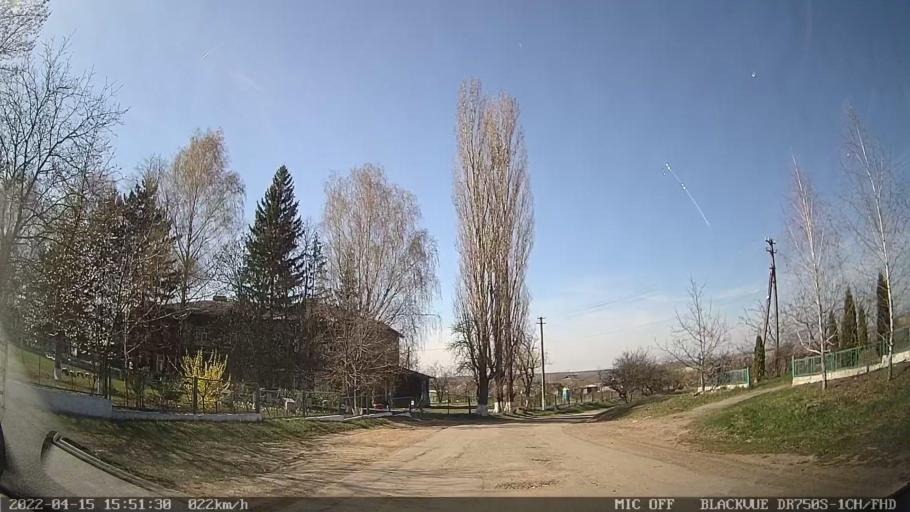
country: MD
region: Raionul Ocnita
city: Otaci
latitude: 48.3945
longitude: 27.8979
